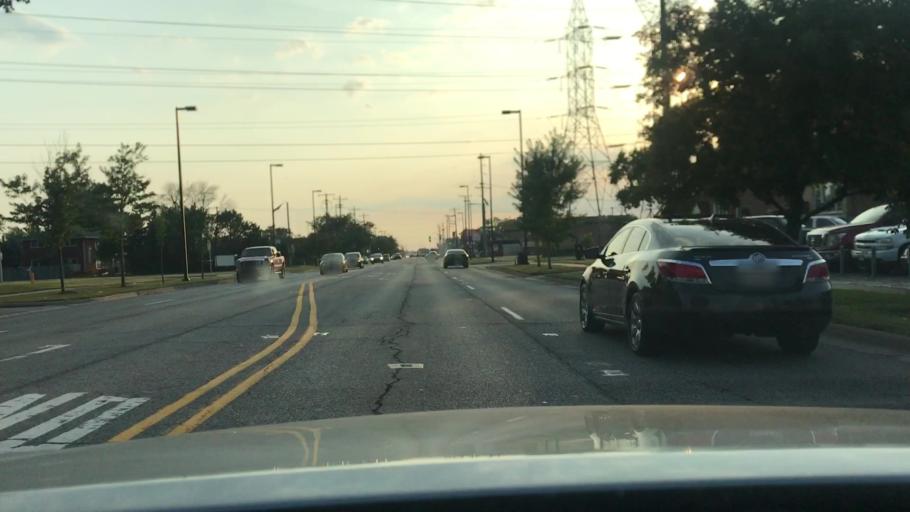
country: US
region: Illinois
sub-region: Cook County
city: Bridgeview
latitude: 41.7483
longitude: -87.7916
